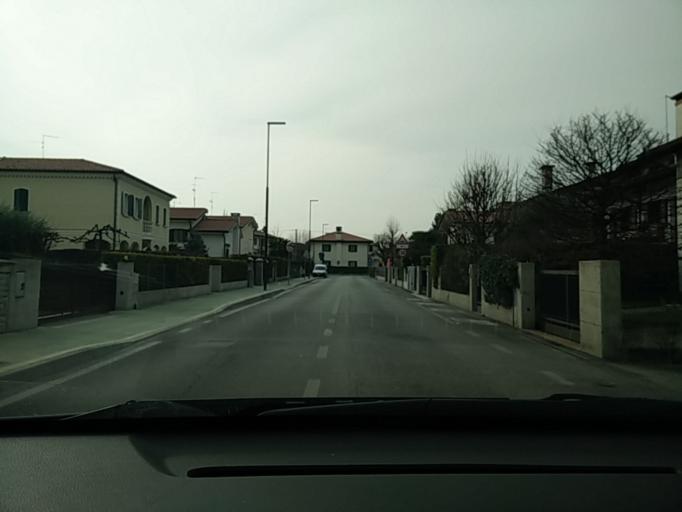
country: IT
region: Veneto
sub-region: Provincia di Venezia
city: San Dona di Piave
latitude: 45.6151
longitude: 12.5686
